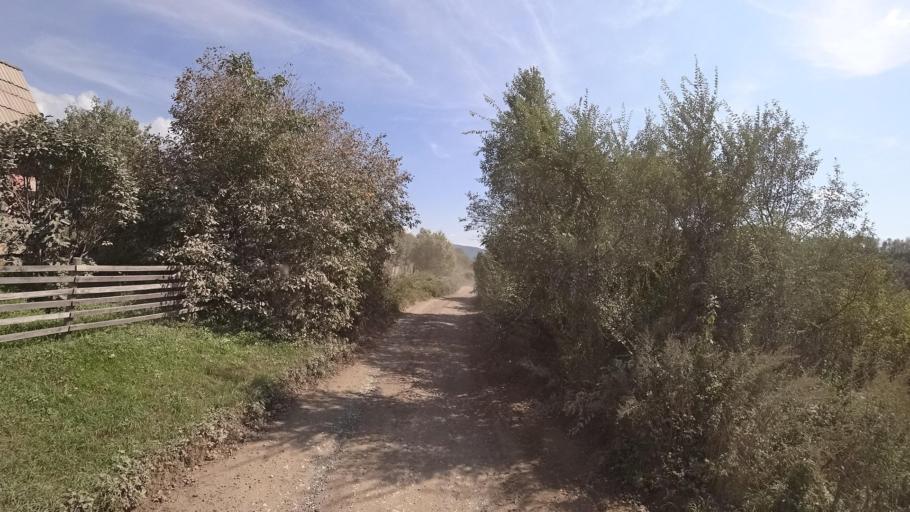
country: RU
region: Jewish Autonomous Oblast
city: Londoko
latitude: 49.0083
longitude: 131.9128
